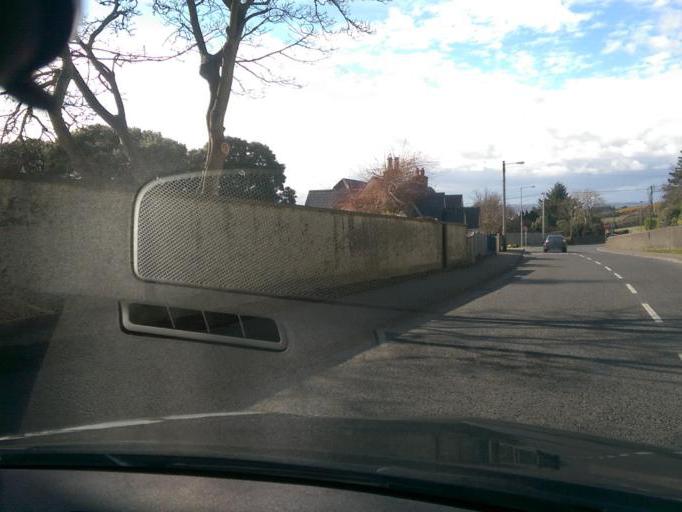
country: IE
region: Leinster
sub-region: Fingal County
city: Howth
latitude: 53.3664
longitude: -6.0773
